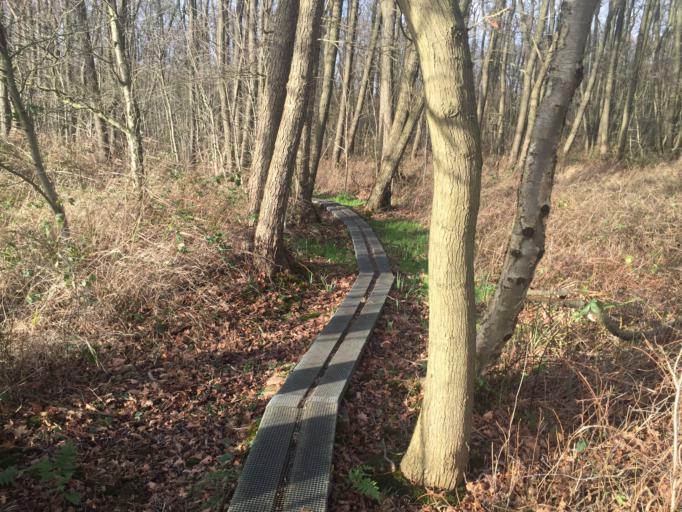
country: NL
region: North Holland
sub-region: Gemeente Bussum
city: Bussum
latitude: 52.2836
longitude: 5.1358
